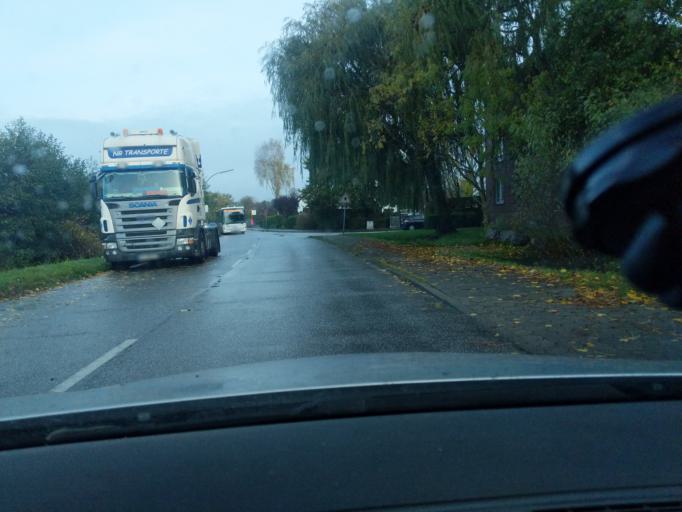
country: DE
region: Lower Saxony
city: Neu Wulmstorf
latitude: 53.5205
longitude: 9.7799
